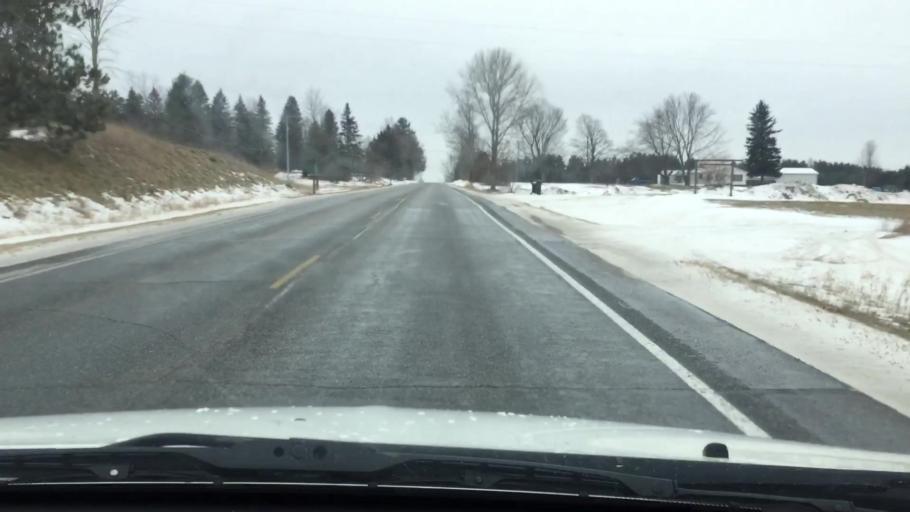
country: US
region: Michigan
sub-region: Wexford County
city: Cadillac
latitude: 44.0701
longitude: -85.4440
